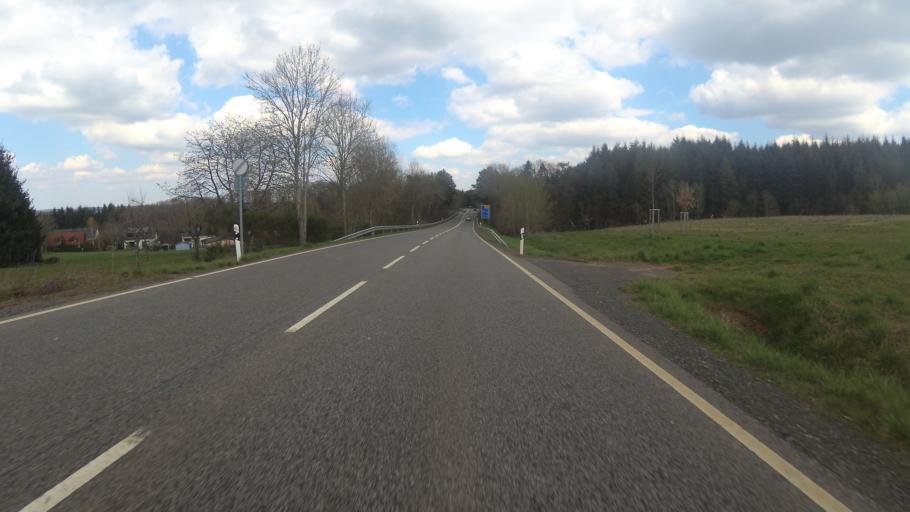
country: DE
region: Rheinland-Pfalz
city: Hasborn
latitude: 50.0399
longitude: 6.9116
